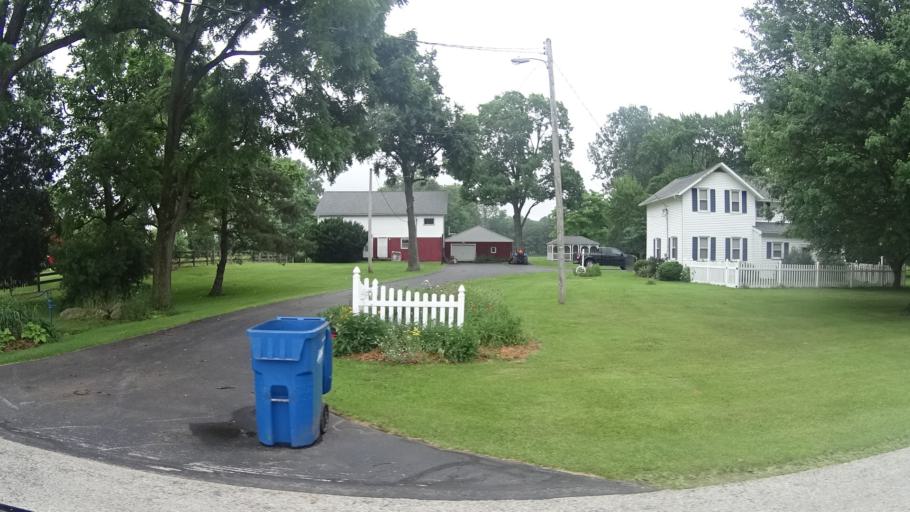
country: US
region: Ohio
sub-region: Erie County
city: Milan
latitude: 41.2896
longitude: -82.5510
